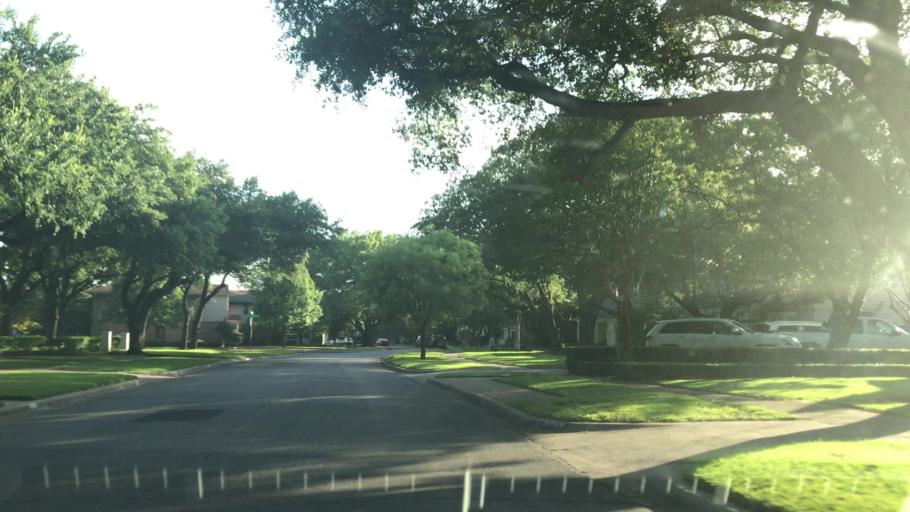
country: US
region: Texas
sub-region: Dallas County
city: University Park
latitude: 32.8317
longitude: -96.8213
